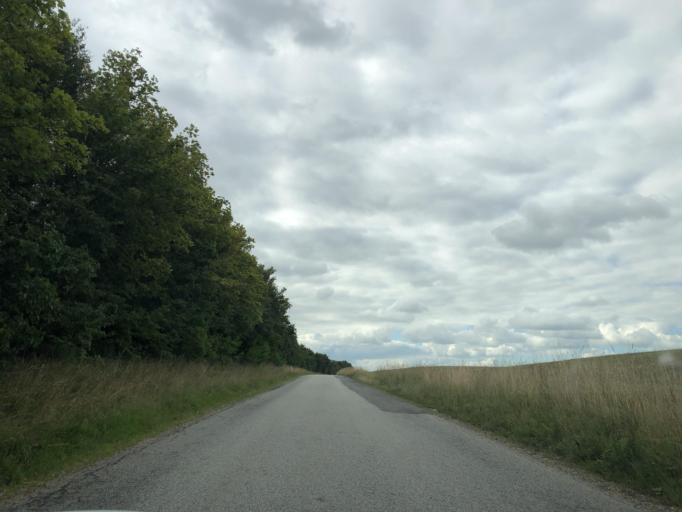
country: DK
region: North Denmark
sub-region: Rebild Kommune
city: Stovring
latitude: 56.9262
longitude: 9.7919
